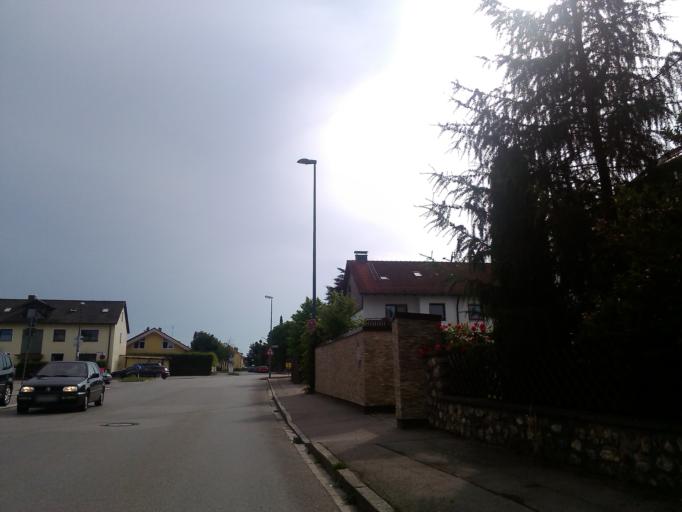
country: DE
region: Bavaria
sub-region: Upper Bavaria
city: Gilching
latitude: 48.1175
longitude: 11.2882
